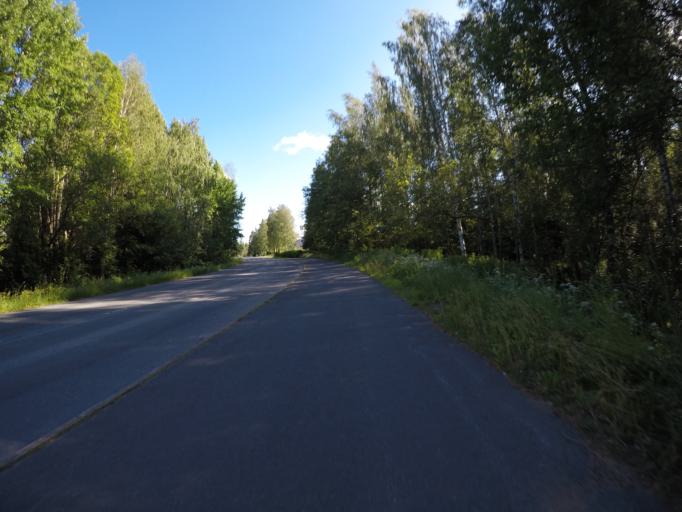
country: FI
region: Haeme
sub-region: Haemeenlinna
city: Haemeenlinna
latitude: 61.0159
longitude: 24.4982
